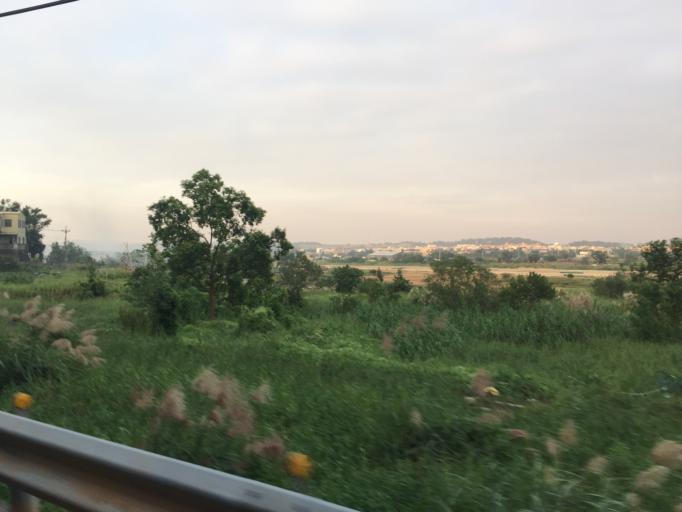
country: TW
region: Taiwan
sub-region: Miaoli
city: Miaoli
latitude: 24.4793
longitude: 120.7768
